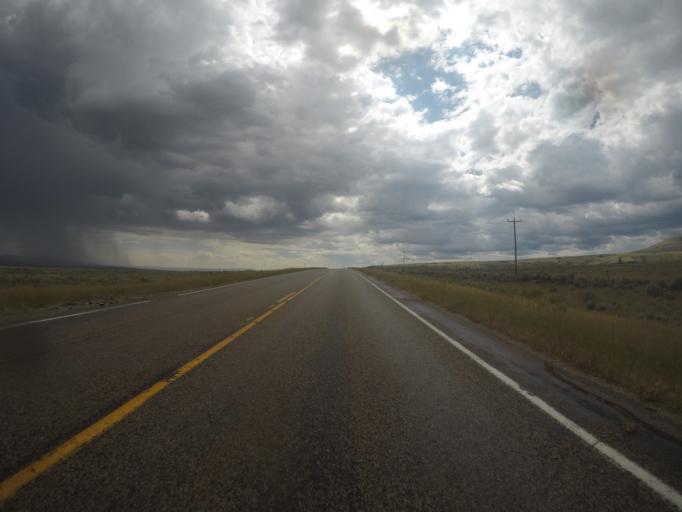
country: US
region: Utah
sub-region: Daggett County
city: Manila
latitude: 41.0221
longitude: -109.9007
